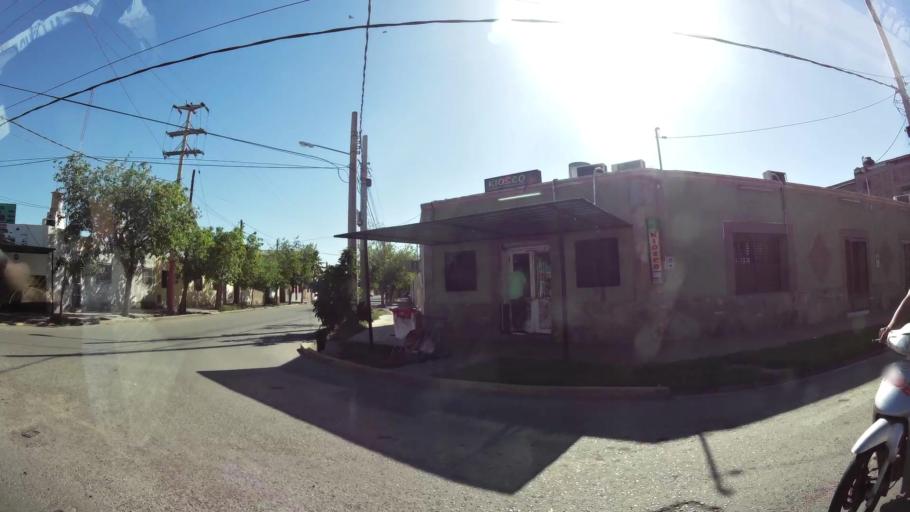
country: AR
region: San Juan
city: Villa Paula de Sarmiento
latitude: -31.5147
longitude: -68.5244
